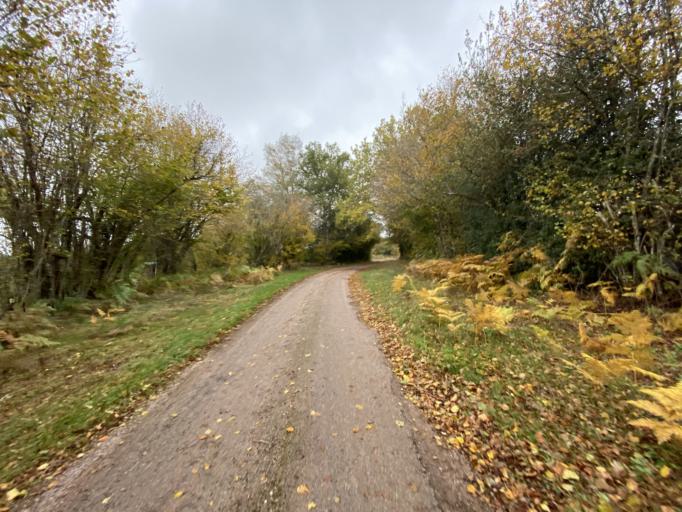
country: FR
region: Bourgogne
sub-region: Departement de la Cote-d'Or
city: Saulieu
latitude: 47.2723
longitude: 4.1622
